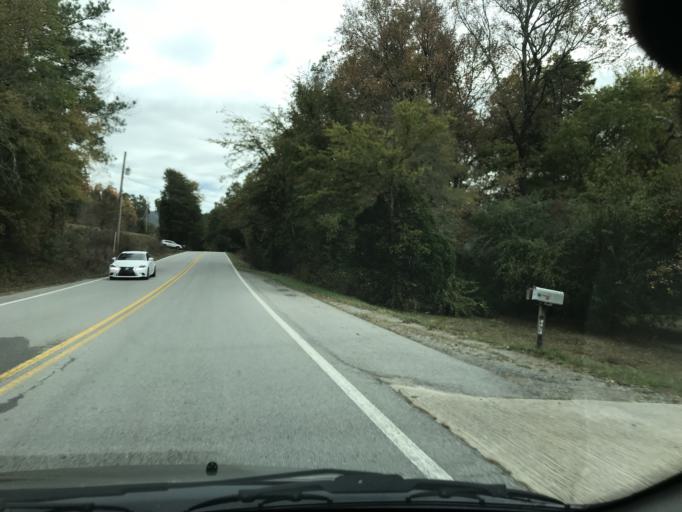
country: US
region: Tennessee
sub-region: Hamilton County
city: Lakesite
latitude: 35.1843
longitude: -85.0585
